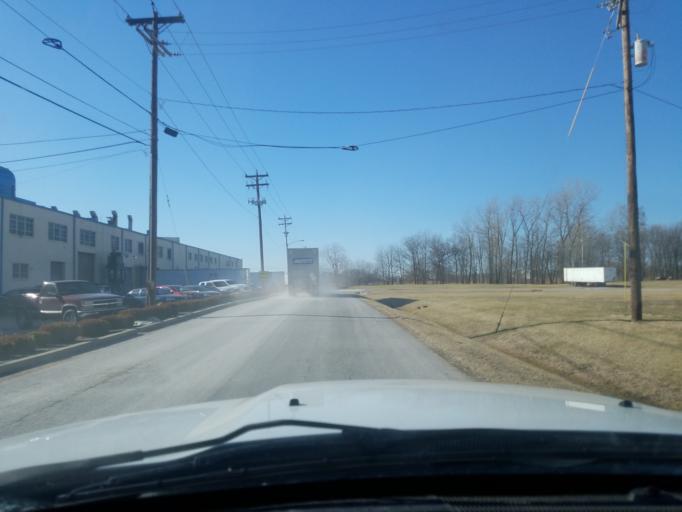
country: US
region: Kentucky
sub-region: Henderson County
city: Henderson
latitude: 37.8050
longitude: -87.6411
